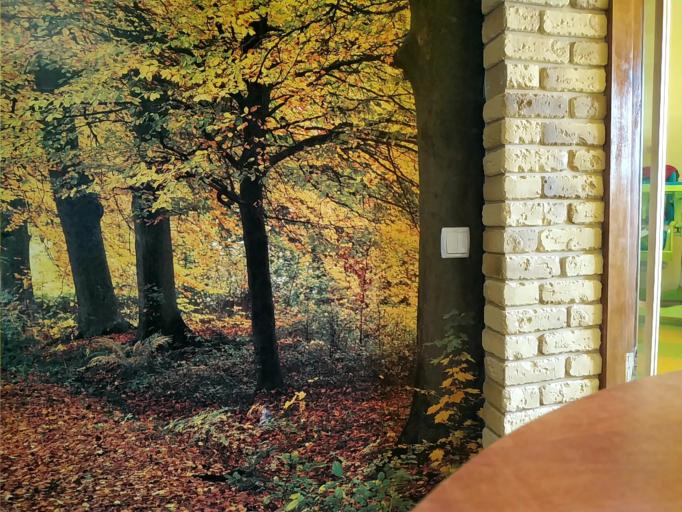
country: RU
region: Vologda
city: Nelazskoye
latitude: 59.4184
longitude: 37.6083
